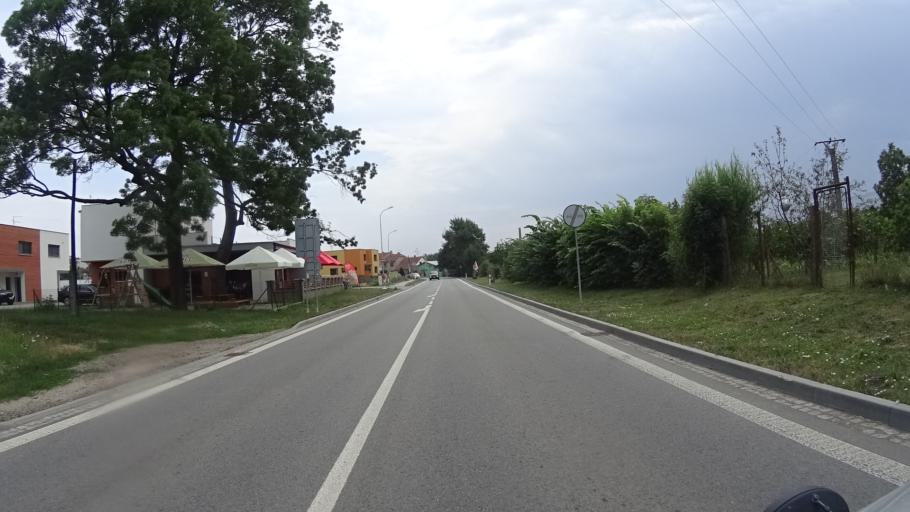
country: CZ
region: South Moravian
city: Podivin
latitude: 48.8220
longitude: 16.8440
